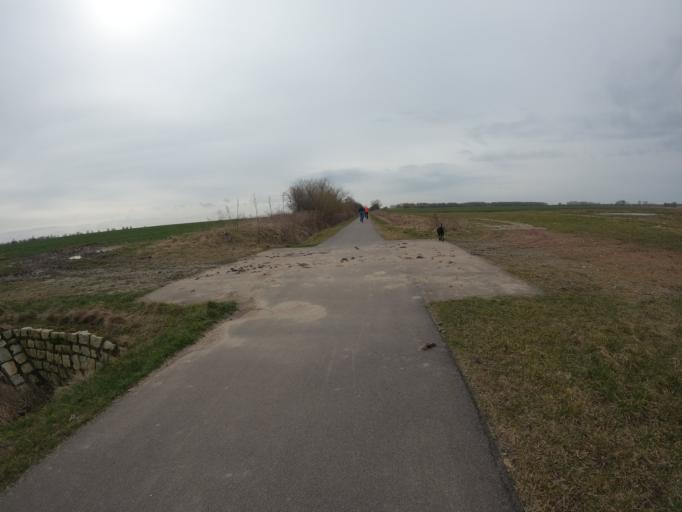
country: PL
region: West Pomeranian Voivodeship
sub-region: Powiat gryficki
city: Mrzezyno
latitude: 54.1166
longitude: 15.3035
